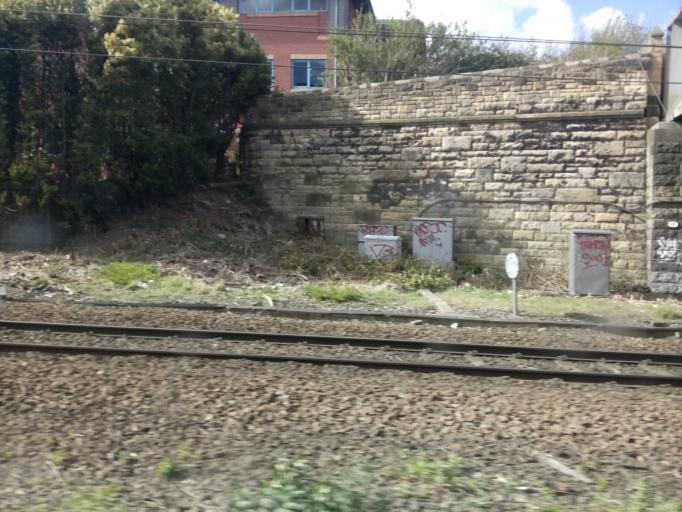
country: GB
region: England
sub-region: Newcastle upon Tyne
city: Newcastle upon Tyne
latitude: 54.9734
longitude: -1.6036
